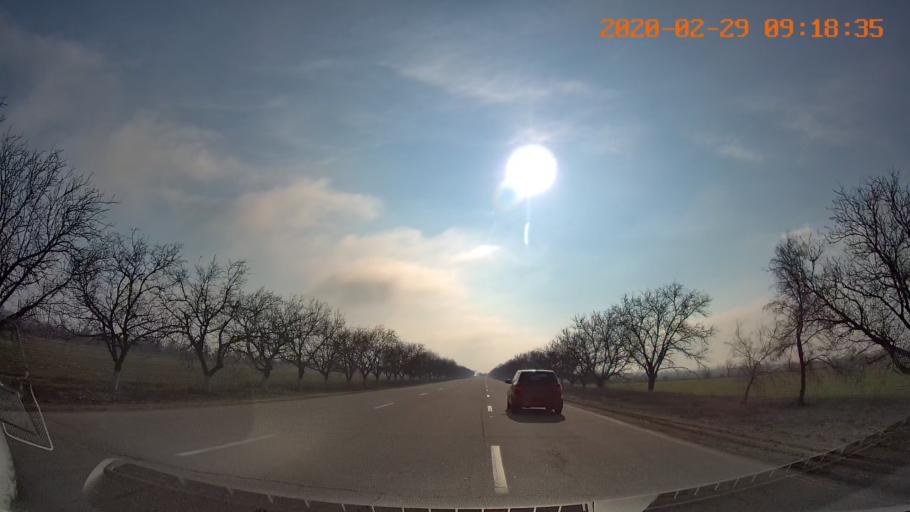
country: MD
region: Telenesti
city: Pervomaisc
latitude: 46.7723
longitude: 29.9255
